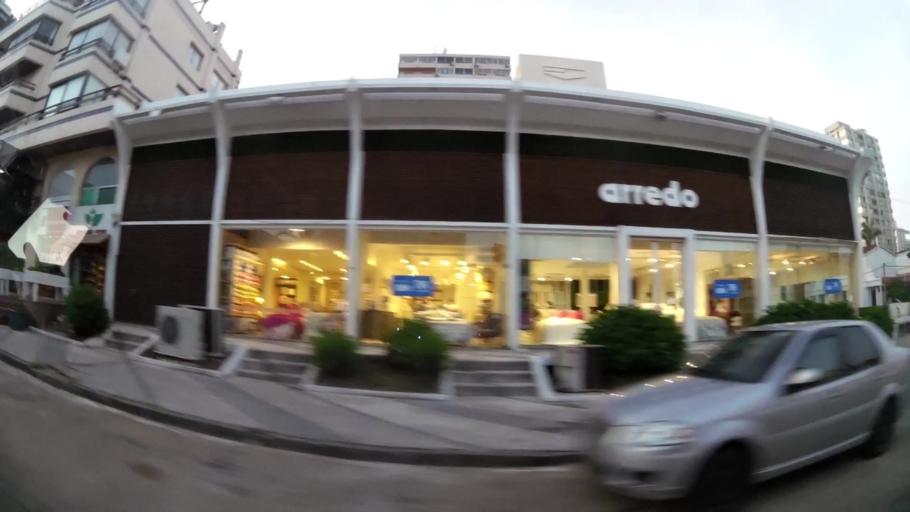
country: UY
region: Maldonado
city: Punta del Este
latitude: -34.9618
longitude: -54.9415
